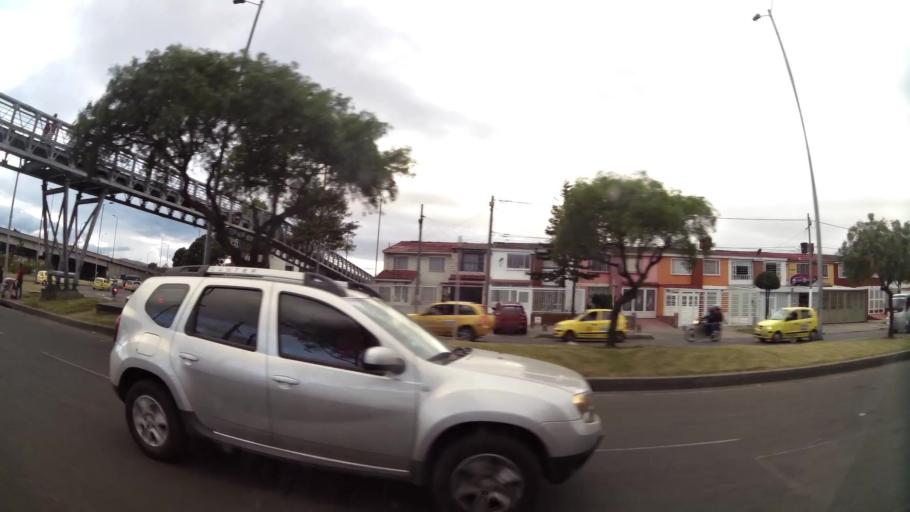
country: CO
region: Bogota D.C.
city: Bogota
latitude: 4.5945
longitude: -74.1264
